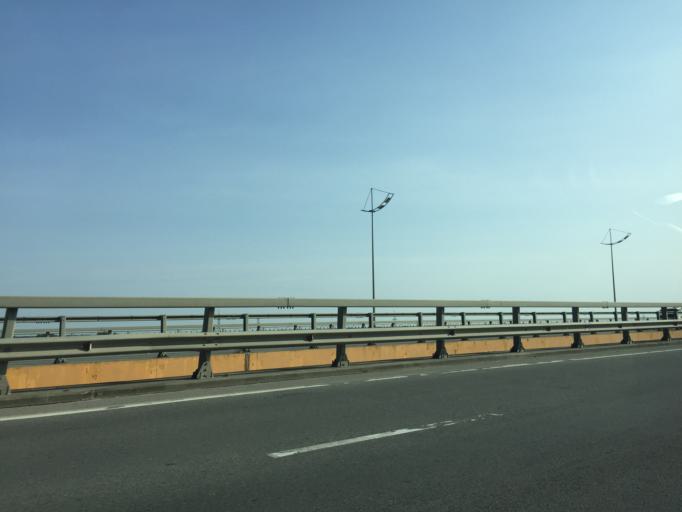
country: RU
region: Kaliningrad
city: Bol'shoe Isakovo
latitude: 54.6943
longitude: 20.5983
